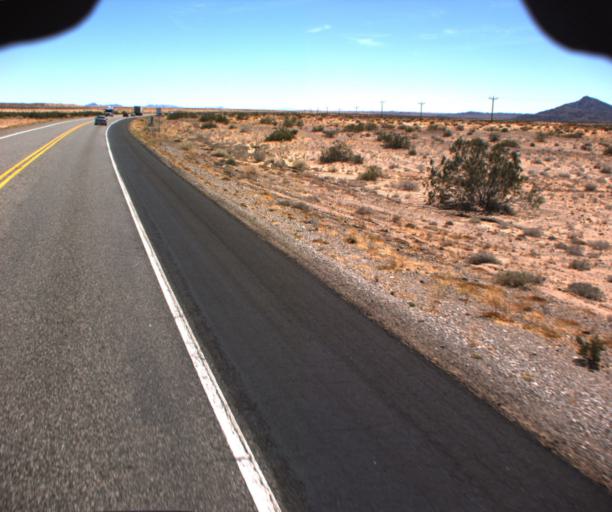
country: US
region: Arizona
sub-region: La Paz County
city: Parker
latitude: 34.0709
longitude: -114.2600
